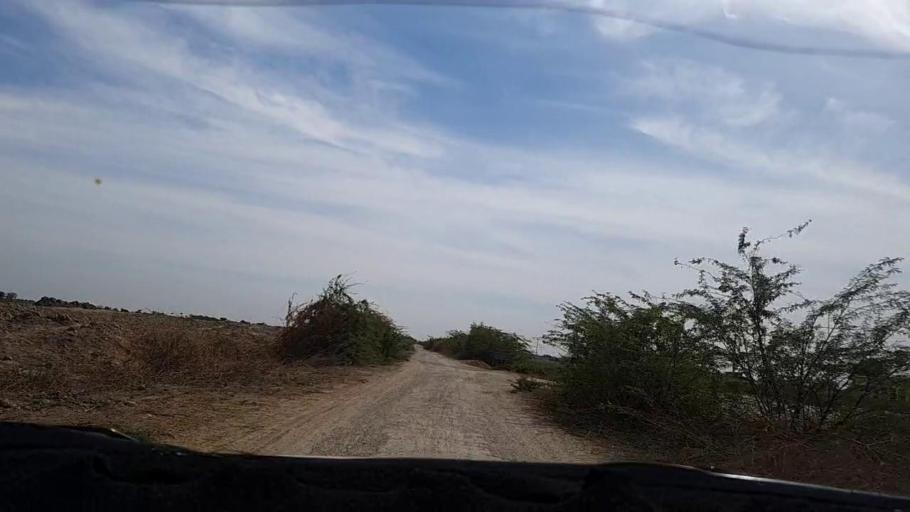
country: PK
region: Sindh
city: Pithoro
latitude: 25.4621
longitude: 69.4556
